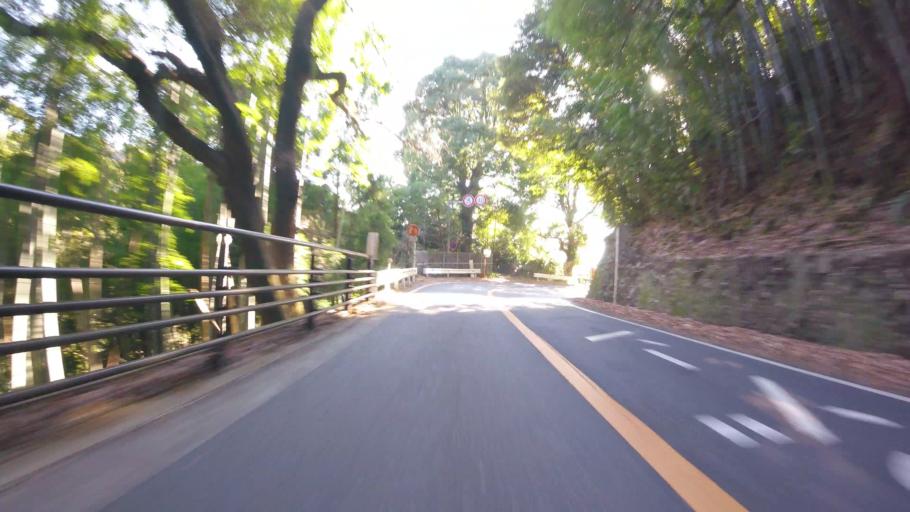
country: JP
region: Shizuoka
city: Atami
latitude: 35.1032
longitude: 139.0647
